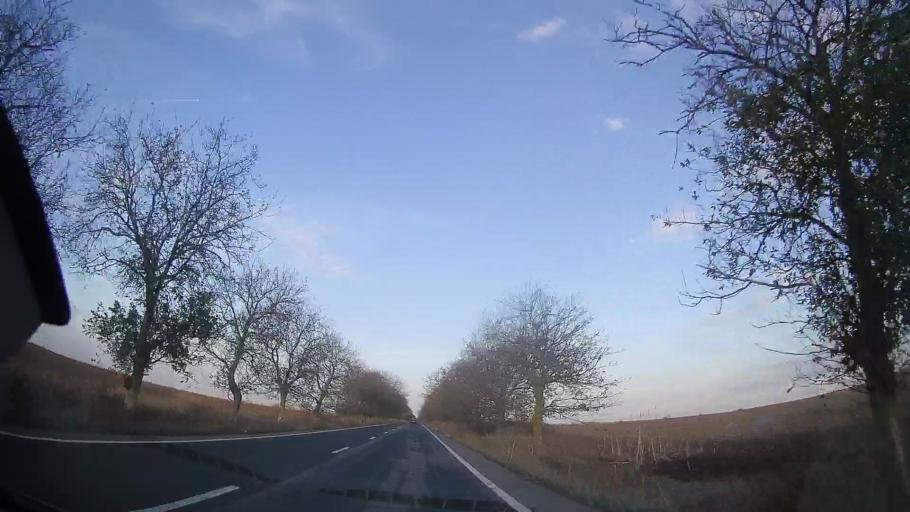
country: RO
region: Constanta
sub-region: Comuna Chirnogeni
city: Chirnogeni
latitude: 43.8669
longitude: 28.2680
